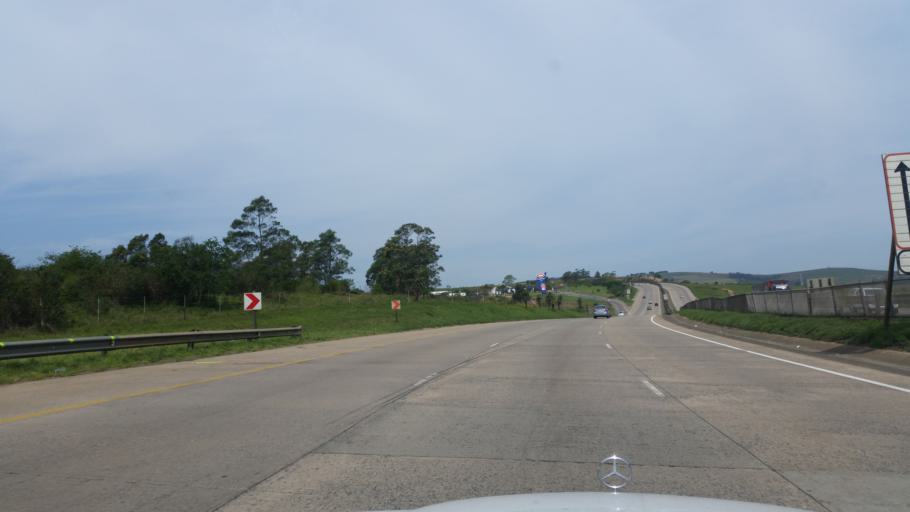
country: ZA
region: KwaZulu-Natal
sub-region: uMgungundlovu District Municipality
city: Camperdown
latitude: -29.7328
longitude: 30.5992
